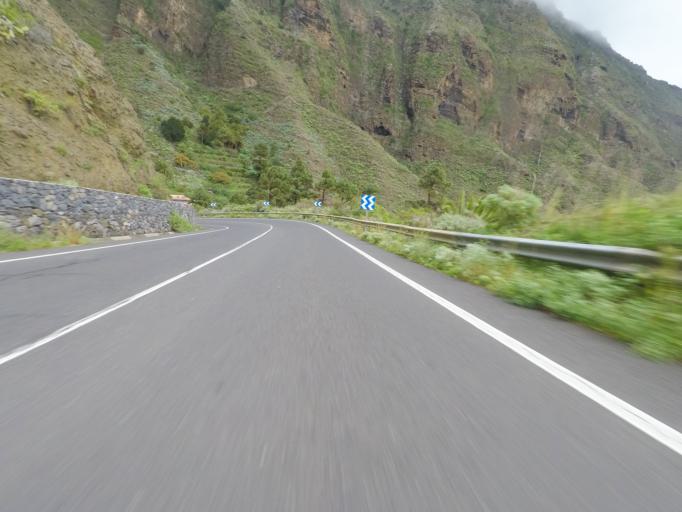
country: ES
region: Canary Islands
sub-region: Provincia de Santa Cruz de Tenerife
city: Hermigua
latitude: 28.1311
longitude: -17.1829
